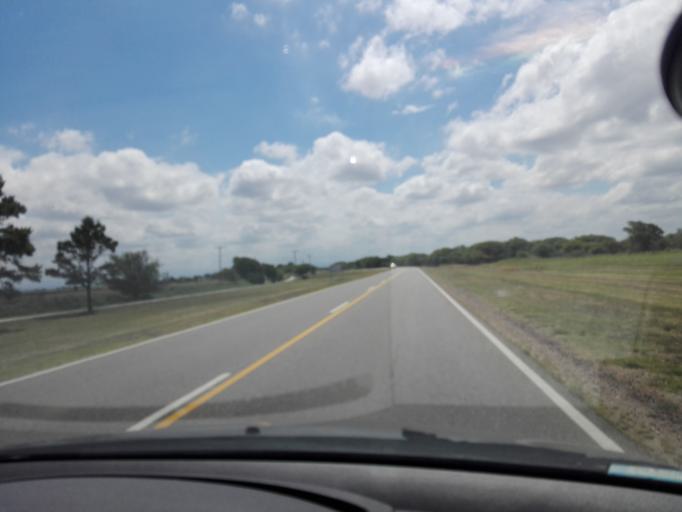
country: AR
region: Cordoba
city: Toledo
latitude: -31.6487
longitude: -64.0992
